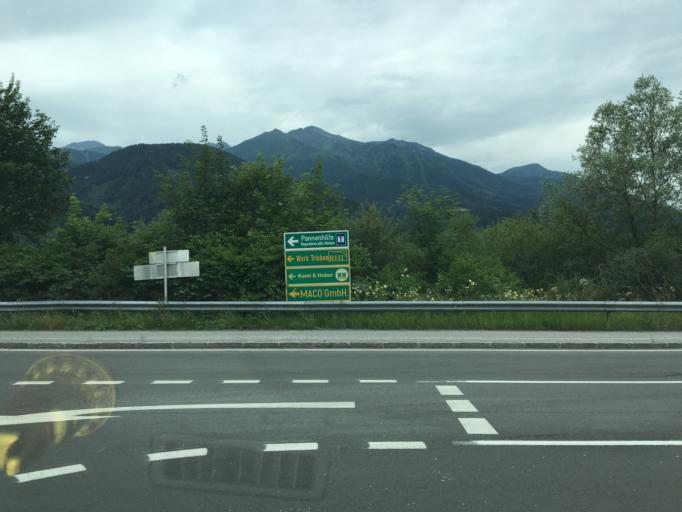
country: AT
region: Styria
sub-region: Politischer Bezirk Liezen
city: Trieben
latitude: 47.4987
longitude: 14.4833
